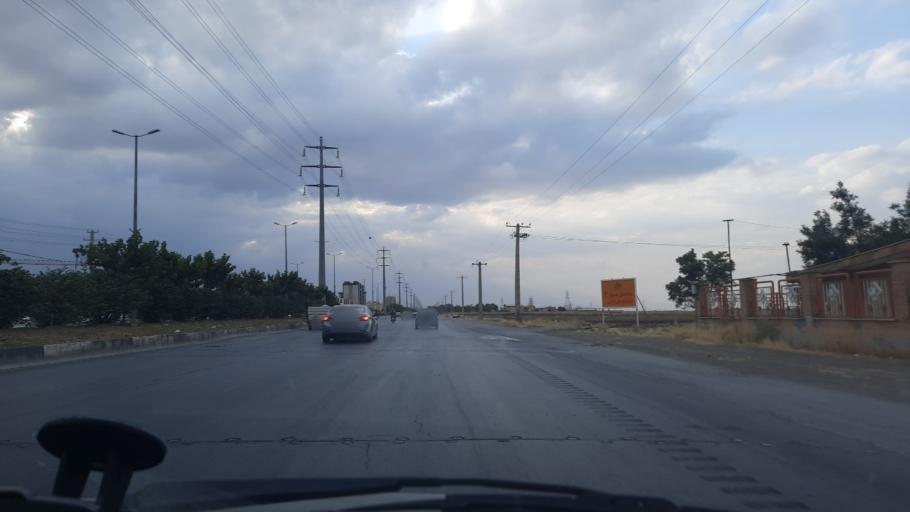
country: IR
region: Markazi
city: Arak
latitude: 34.1014
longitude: 49.7501
